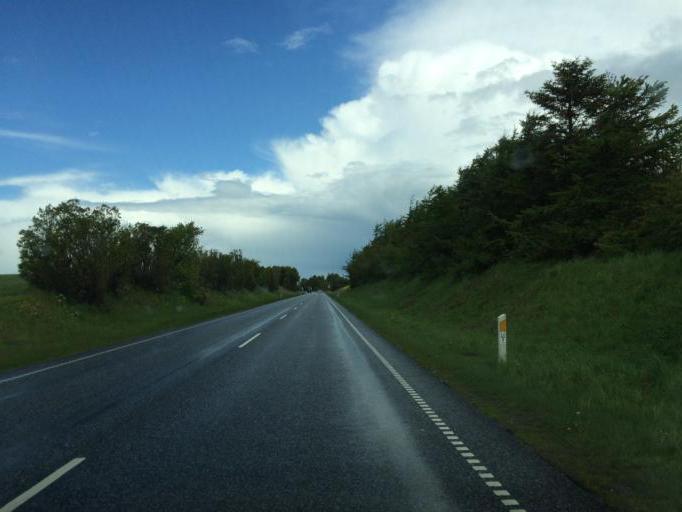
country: DK
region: North Denmark
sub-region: Vesthimmerland Kommune
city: Farso
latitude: 56.6224
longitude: 9.3508
